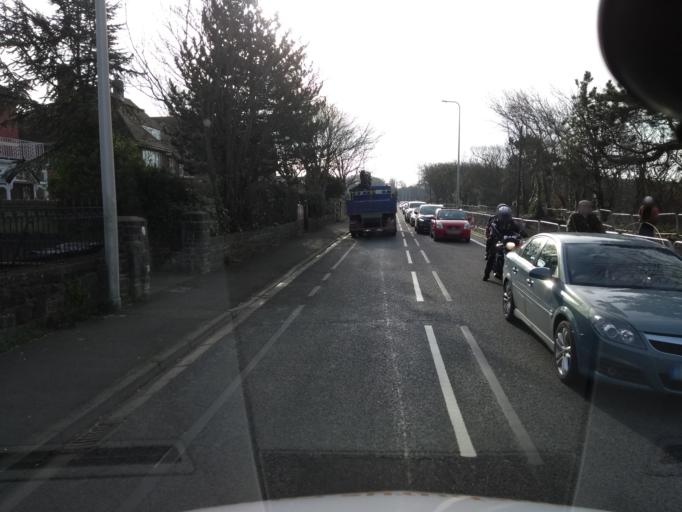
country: GB
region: England
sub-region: North Somerset
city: Weston-super-Mare
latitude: 51.3312
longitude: -2.9810
